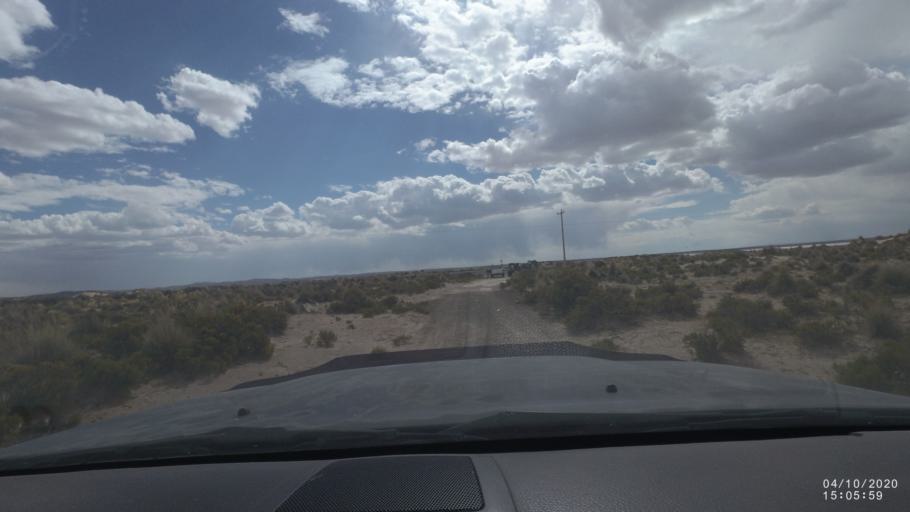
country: BO
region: Oruro
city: Poopo
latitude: -18.6935
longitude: -67.5564
